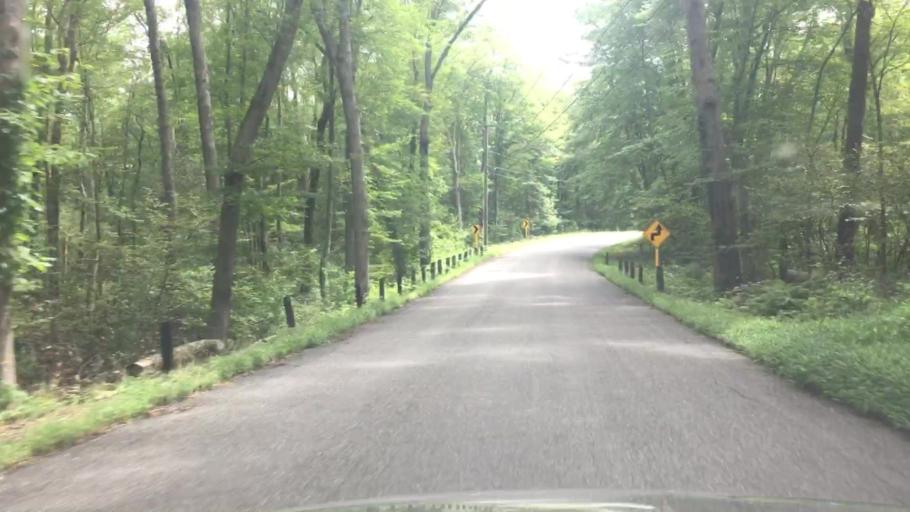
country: US
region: Connecticut
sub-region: Tolland County
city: Storrs
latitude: 41.8927
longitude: -72.1738
